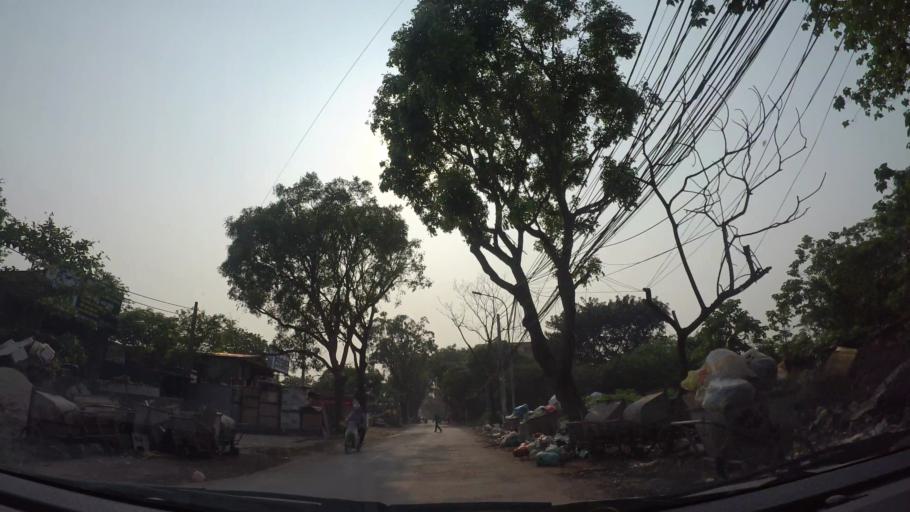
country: VN
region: Ha Noi
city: Ha Dong
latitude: 20.9957
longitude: 105.7514
